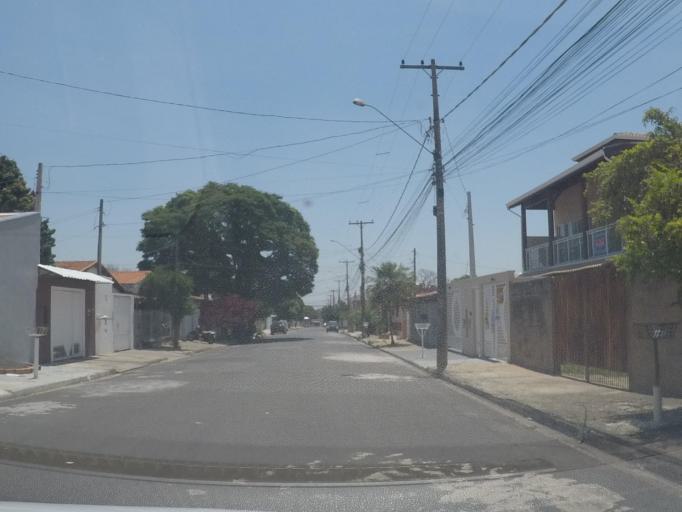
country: BR
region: Sao Paulo
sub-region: Hortolandia
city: Hortolandia
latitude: -22.8578
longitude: -47.1812
